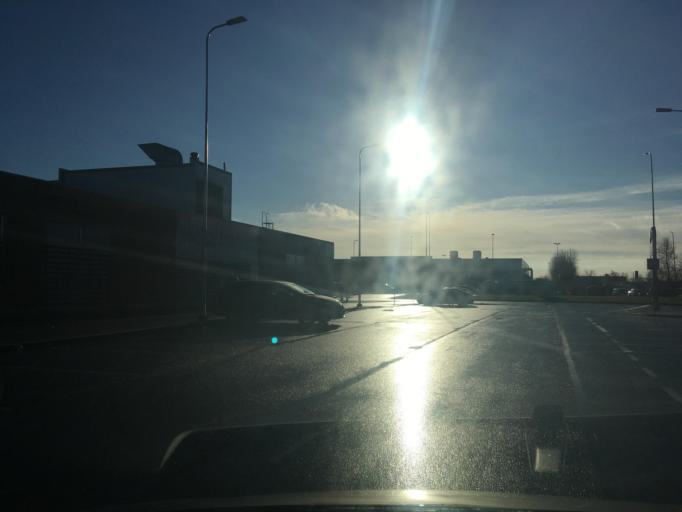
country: EE
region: Ida-Virumaa
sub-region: Narva linn
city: Narva
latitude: 59.3658
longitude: 28.1864
